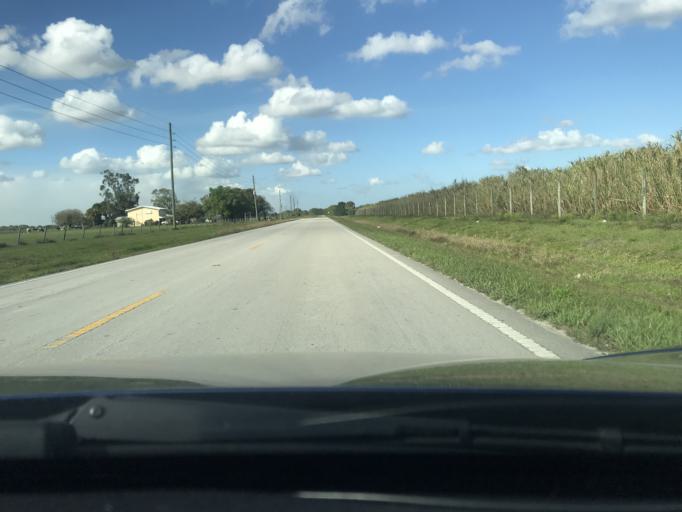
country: US
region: Florida
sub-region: Okeechobee County
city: Taylor Creek
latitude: 27.2695
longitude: -80.6946
